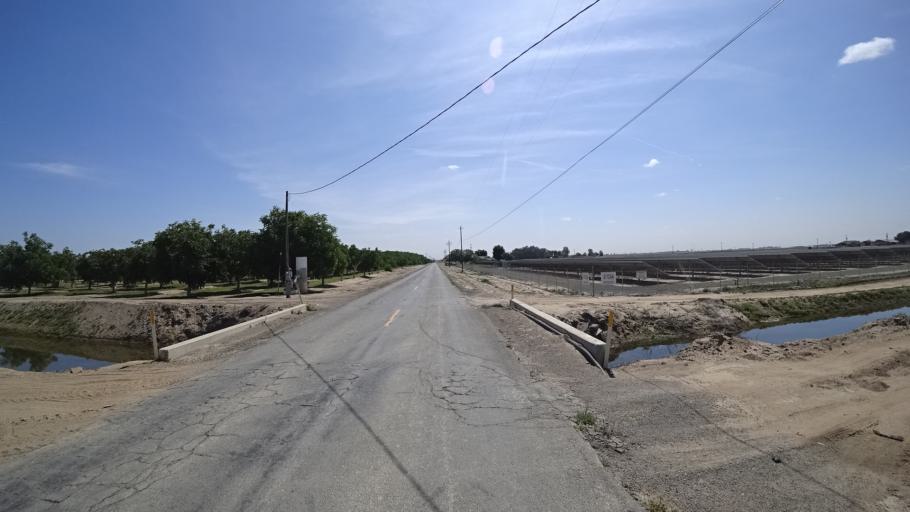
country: US
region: California
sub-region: Kings County
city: Armona
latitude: 36.2693
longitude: -119.6852
